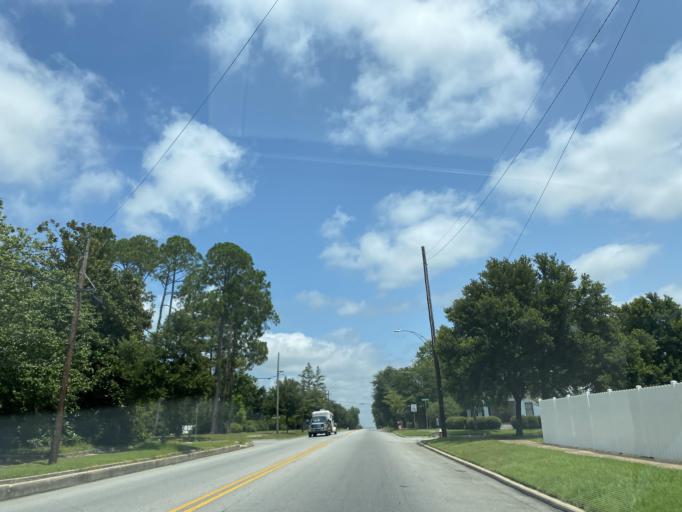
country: US
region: Georgia
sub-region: Telfair County
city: McRae
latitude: 32.0636
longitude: -82.9024
